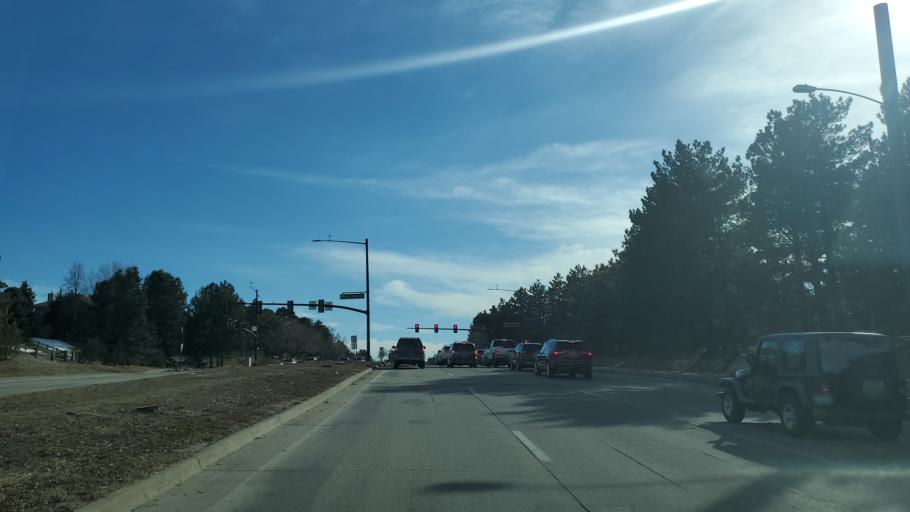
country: US
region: Colorado
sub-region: Douglas County
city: Highlands Ranch
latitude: 39.5615
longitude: -104.9602
